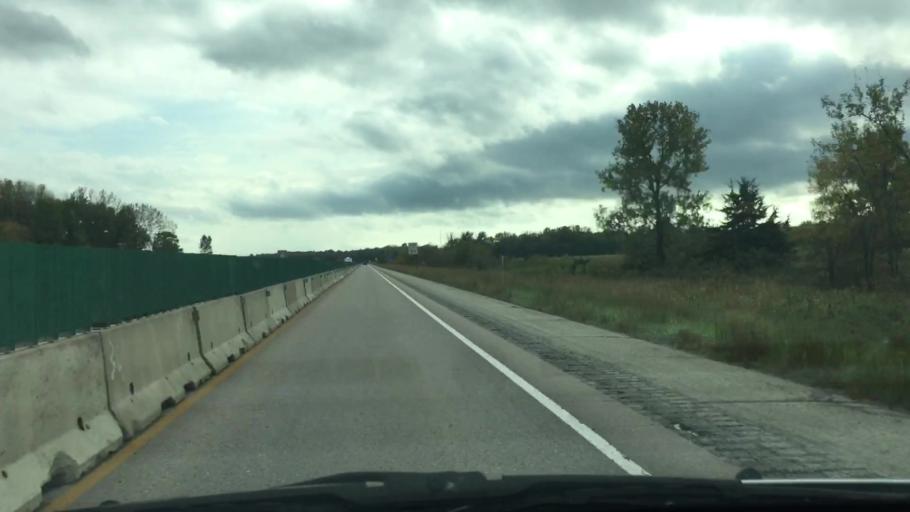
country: US
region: Iowa
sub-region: Decatur County
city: Lamoni
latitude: 40.6772
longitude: -93.8490
